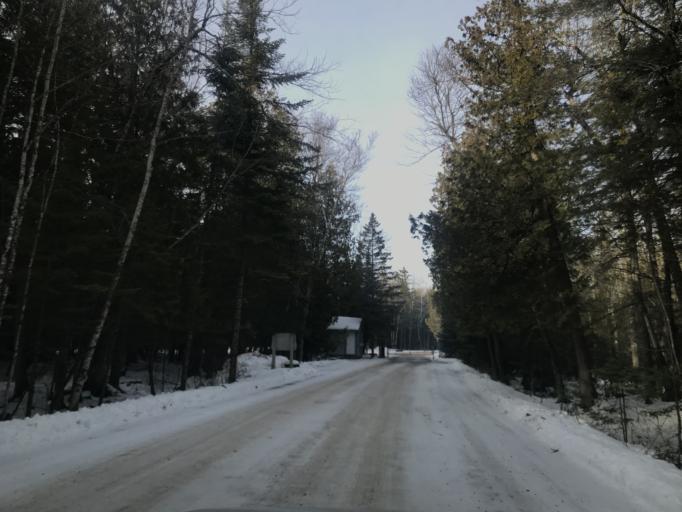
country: US
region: Wisconsin
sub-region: Door County
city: Sturgeon Bay
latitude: 45.1549
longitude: -87.0585
